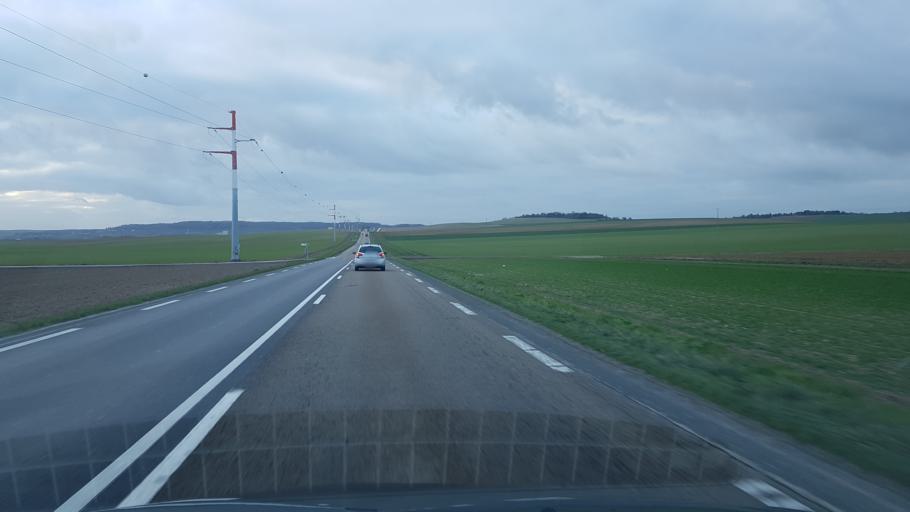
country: FR
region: Champagne-Ardenne
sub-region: Departement de la Marne
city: Sezanne
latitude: 48.7206
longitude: 3.7752
